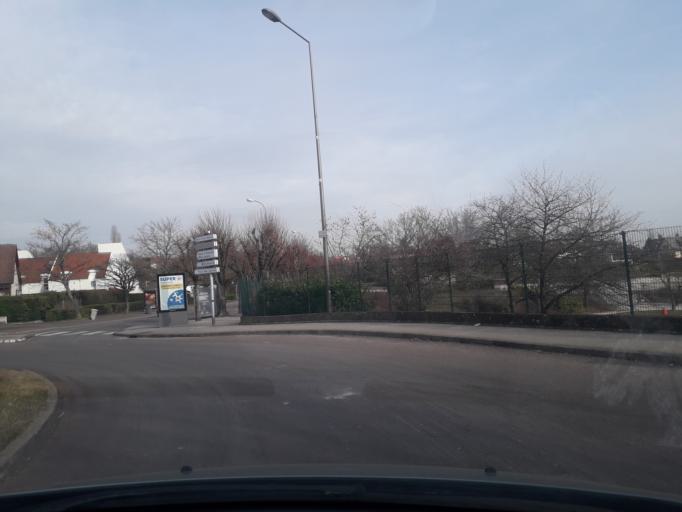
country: FR
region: Bourgogne
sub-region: Departement de la Cote-d'Or
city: Fontaine-les-Dijon
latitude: 47.3390
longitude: 5.0217
